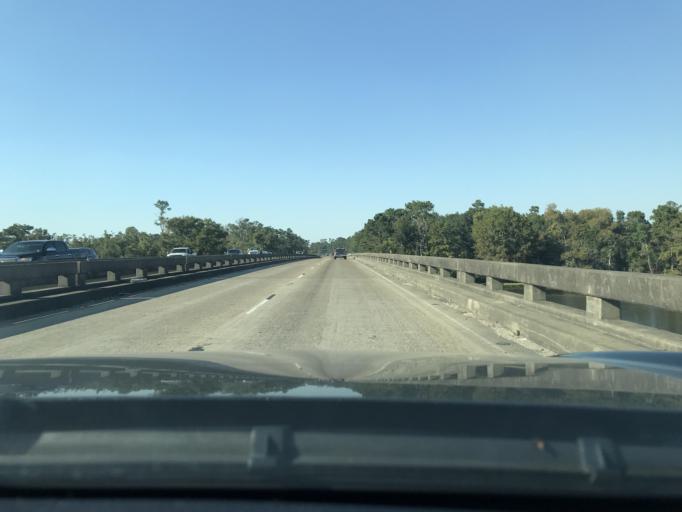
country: US
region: Louisiana
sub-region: Calcasieu Parish
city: Moss Bluff
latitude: 30.2716
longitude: -93.1822
